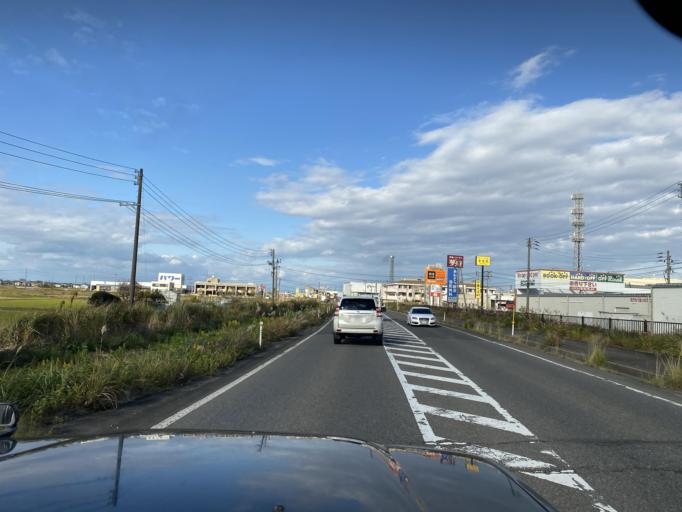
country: JP
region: Niigata
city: Niitsu-honcho
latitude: 37.7848
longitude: 139.1119
